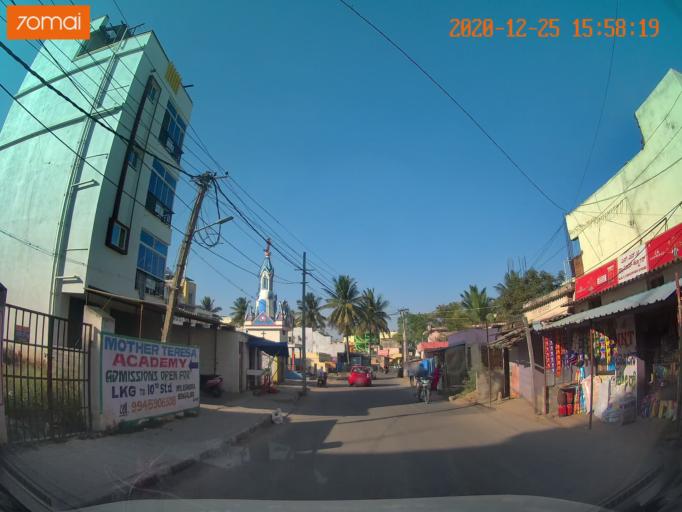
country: IN
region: Karnataka
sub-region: Bangalore Urban
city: Bangalore
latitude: 12.8711
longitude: 77.6244
